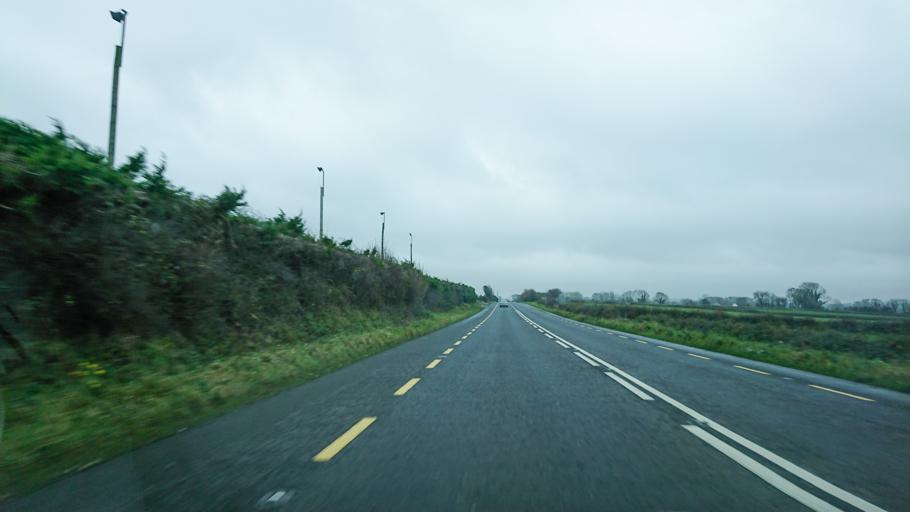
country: IE
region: Leinster
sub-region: Kilkenny
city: Mooncoin
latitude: 52.2879
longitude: -7.2244
